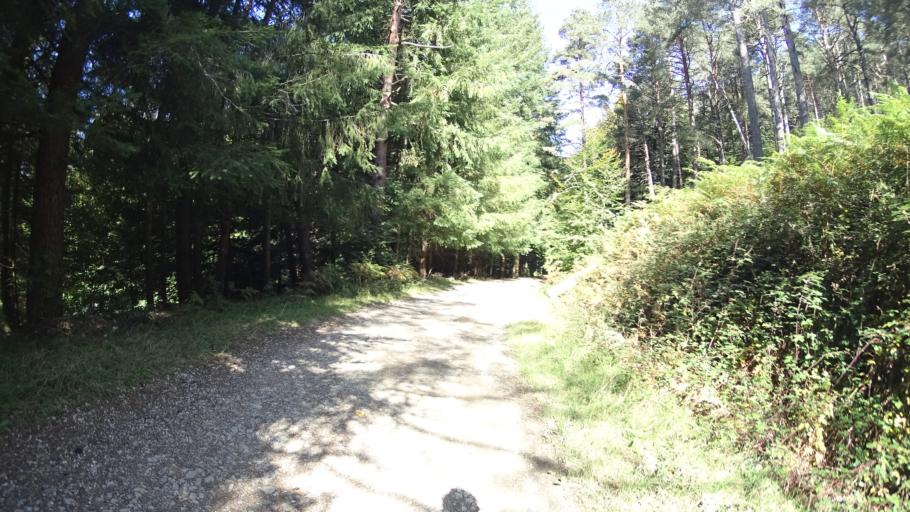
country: ES
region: Navarre
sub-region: Provincia de Navarra
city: Orbara
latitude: 42.9890
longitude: -1.1376
